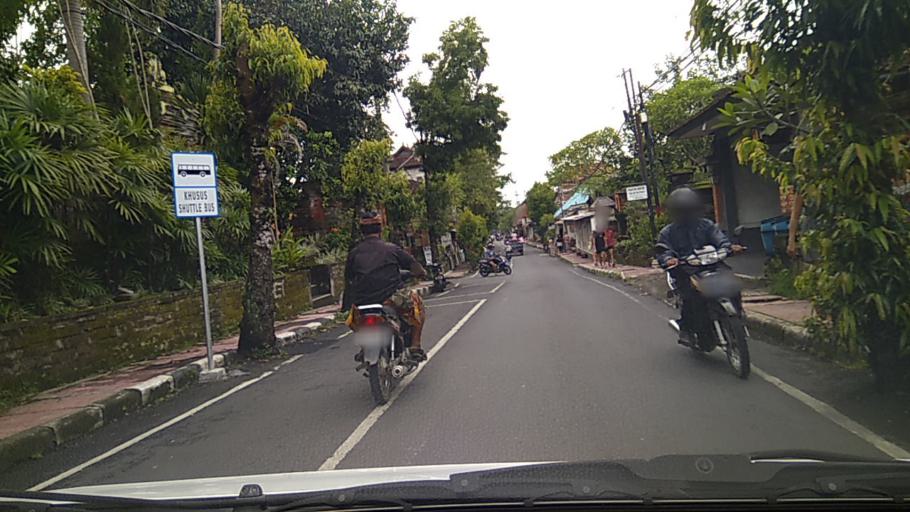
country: ID
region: Bali
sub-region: Kabupaten Gianyar
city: Ubud
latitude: -8.5130
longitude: 115.2642
